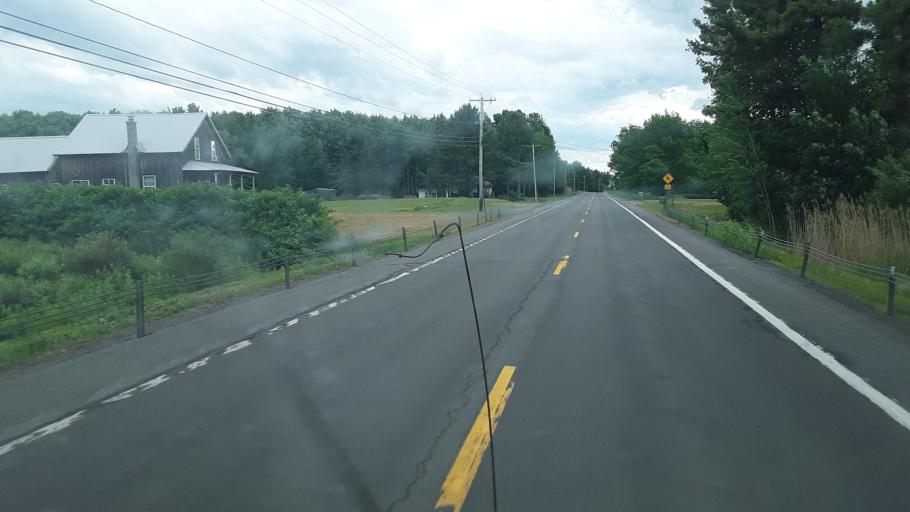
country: US
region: New York
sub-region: Oneida County
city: Rome
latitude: 43.3419
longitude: -75.4760
